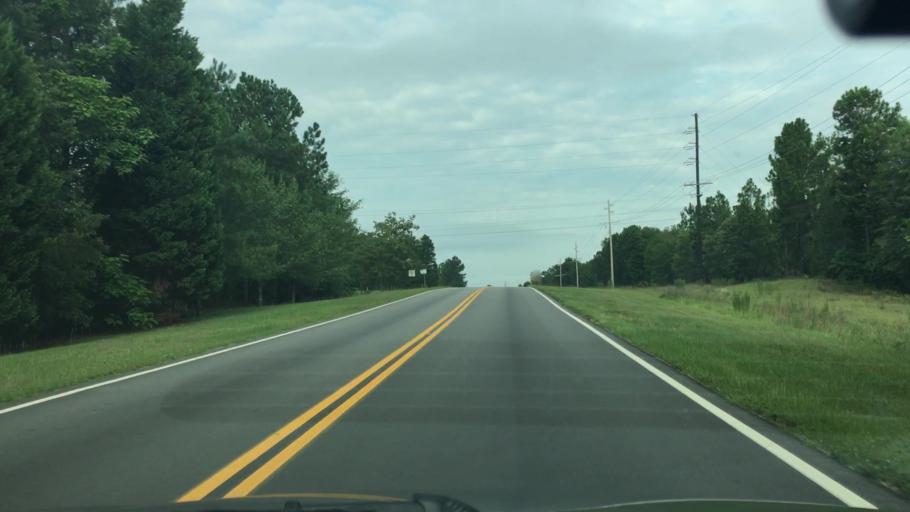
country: US
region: South Carolina
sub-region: Aiken County
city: Aiken
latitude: 33.6540
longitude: -81.6910
